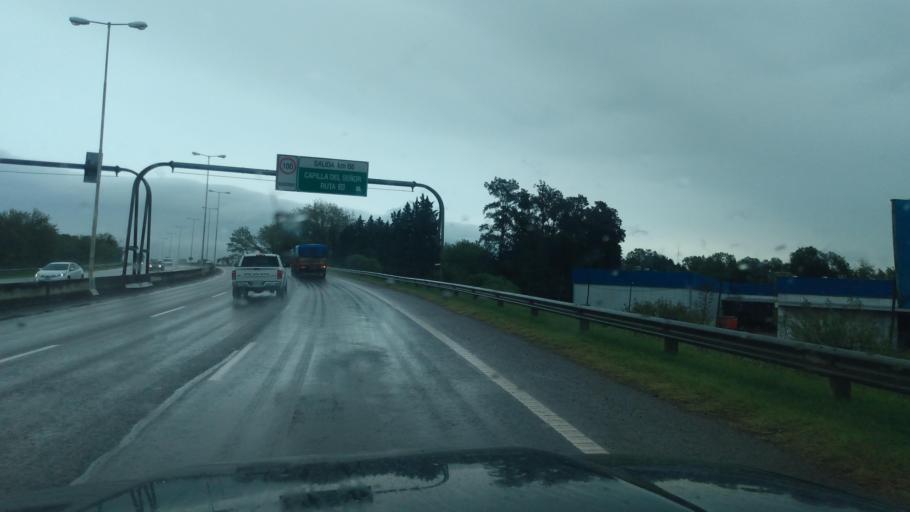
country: AR
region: Buenos Aires
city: Capilla del Senor
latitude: -34.3912
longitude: -59.0289
